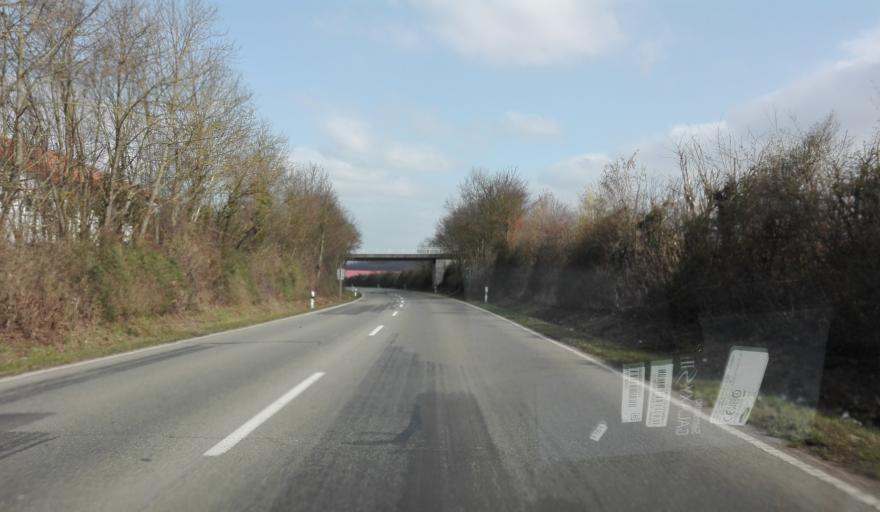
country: DE
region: Rheinland-Pfalz
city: Morstadt
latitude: 49.6589
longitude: 8.2594
